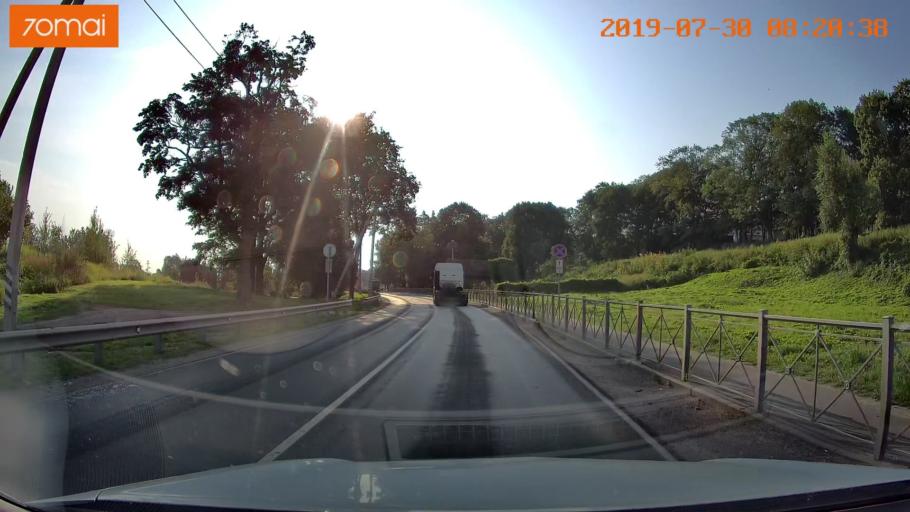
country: RU
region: Kaliningrad
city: Chernyakhovsk
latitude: 54.6264
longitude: 21.5192
